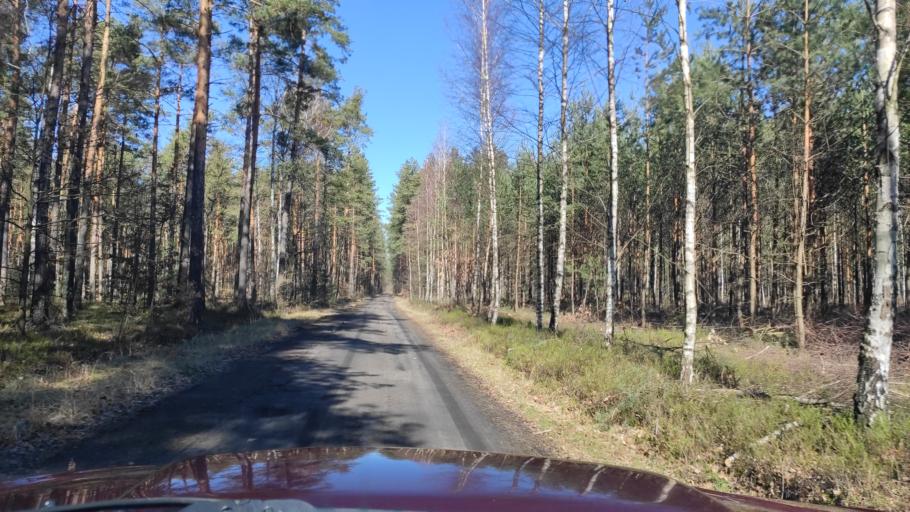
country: PL
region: Masovian Voivodeship
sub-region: Powiat kozienicki
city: Garbatka-Letnisko
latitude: 51.4300
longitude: 21.5485
